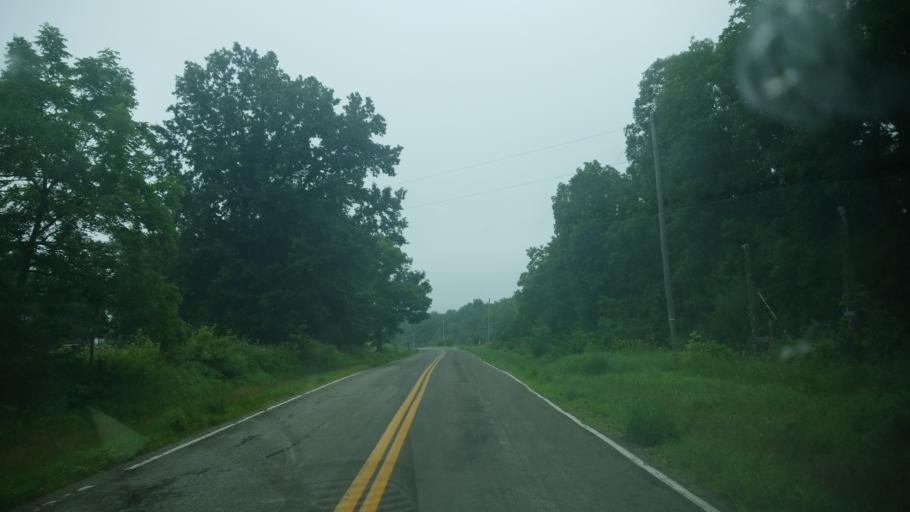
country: US
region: Missouri
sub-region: Audrain County
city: Vandalia
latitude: 39.2937
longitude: -91.3506
